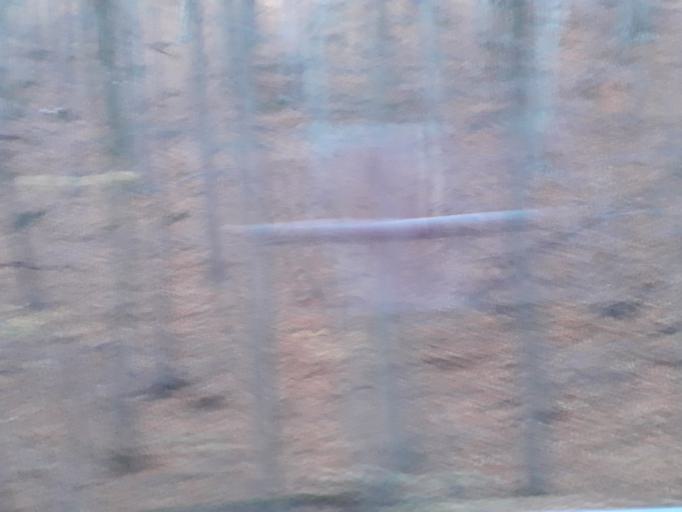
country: DE
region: Saxony
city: Reinhardtsgrimma
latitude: 50.9185
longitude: 13.7848
